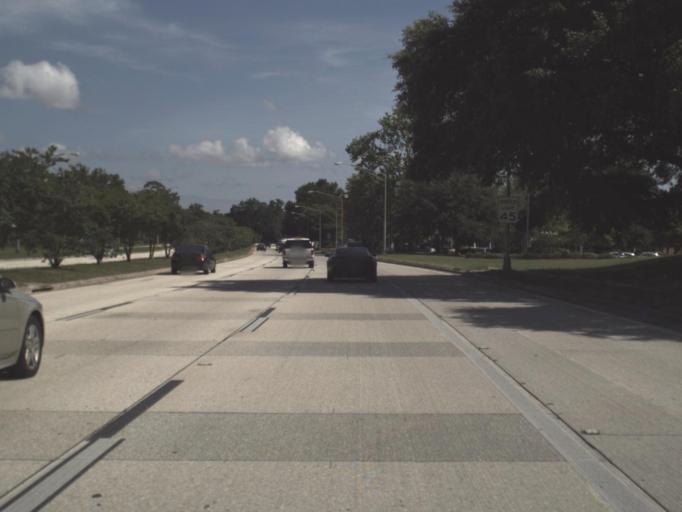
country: US
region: Florida
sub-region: Duval County
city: Jacksonville
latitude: 30.2976
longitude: -81.7199
